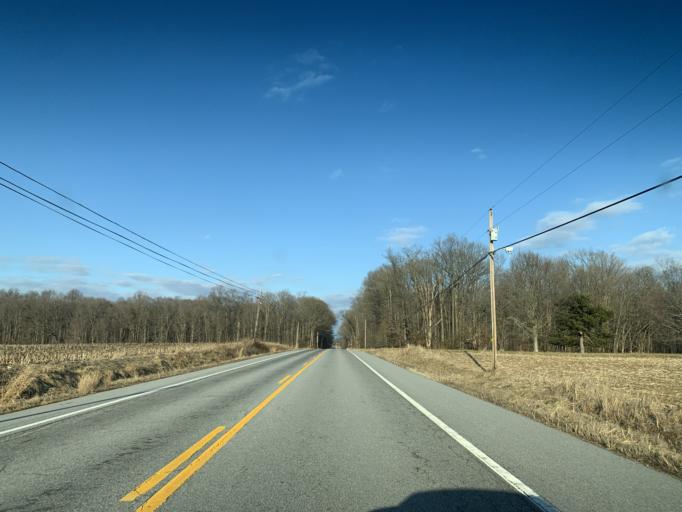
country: US
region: Maryland
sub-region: Queen Anne's County
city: Kingstown
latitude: 39.1573
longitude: -75.9519
